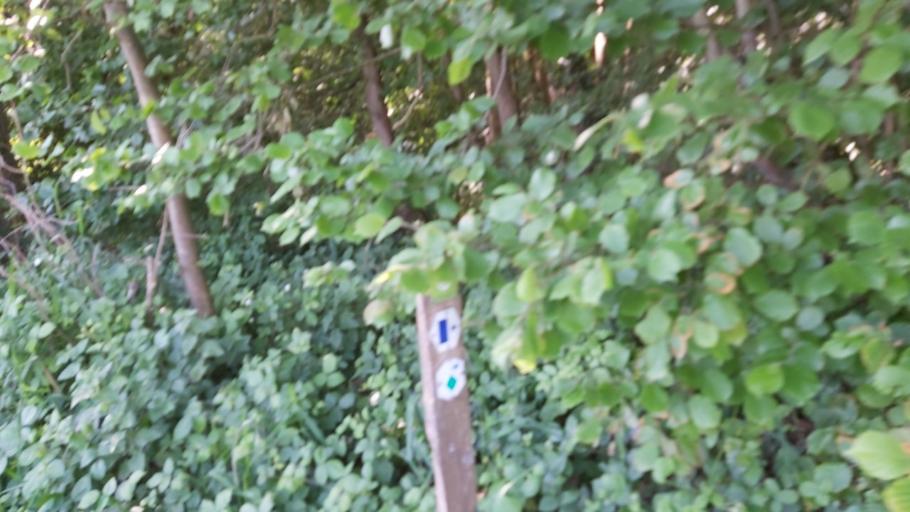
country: BE
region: Flanders
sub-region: Provincie Vlaams-Brabant
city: Glabbeek-Zuurbemde
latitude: 50.8513
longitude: 4.9362
